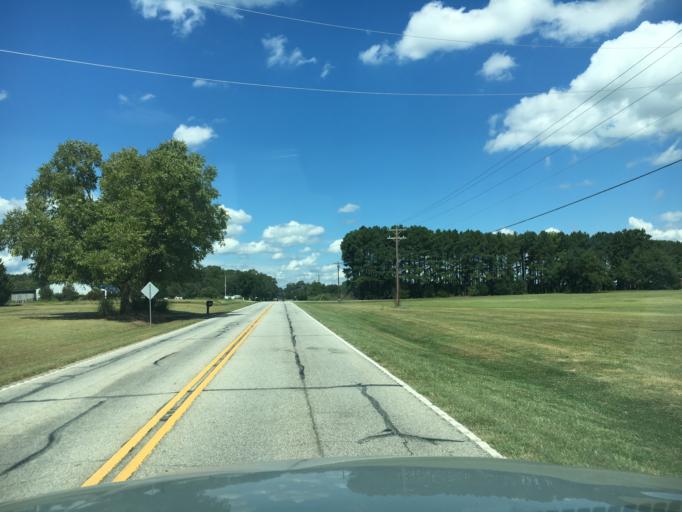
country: US
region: South Carolina
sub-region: Laurens County
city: Laurens
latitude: 34.5026
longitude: -82.0738
